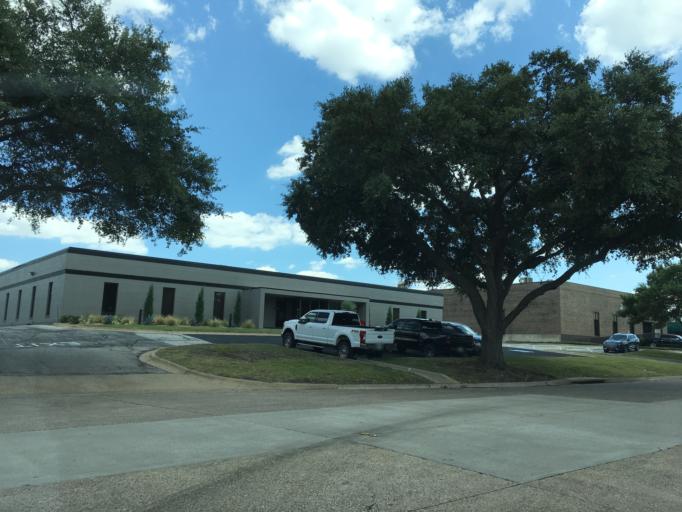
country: US
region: Texas
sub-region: Dallas County
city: Addison
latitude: 32.9459
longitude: -96.8368
